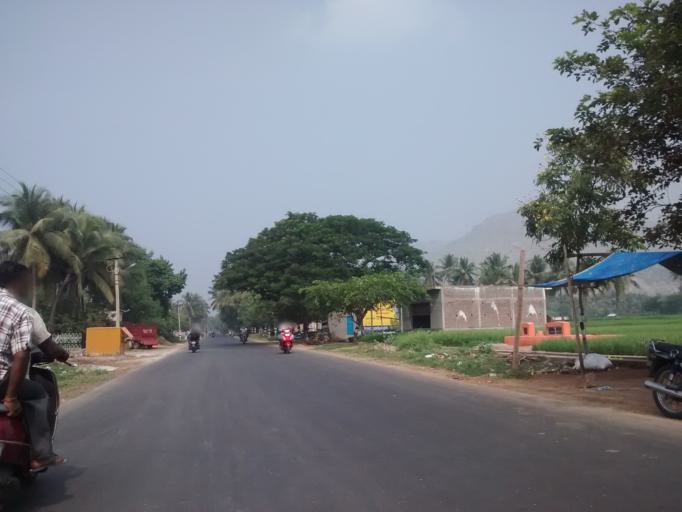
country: IN
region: Tamil Nadu
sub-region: Krishnagiri
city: Kaverippattanam
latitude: 12.4657
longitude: 78.2065
